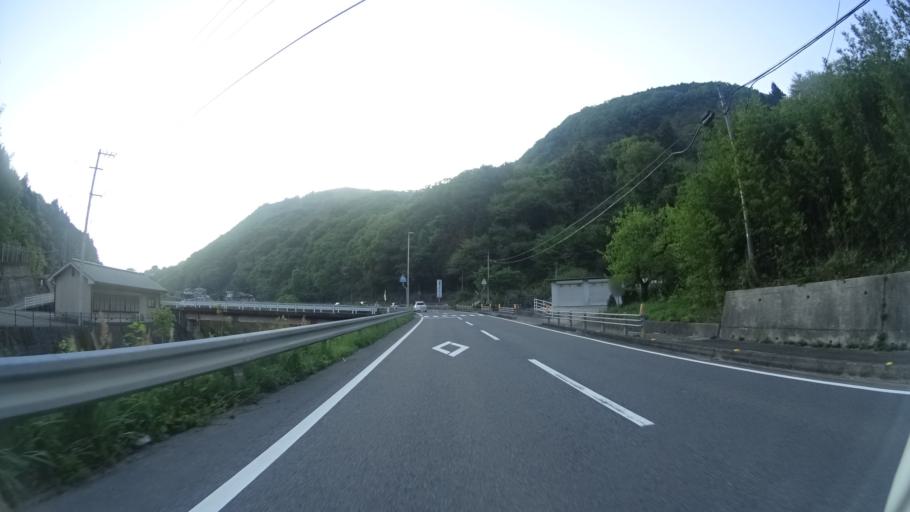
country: JP
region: Tokushima
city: Ikedacho
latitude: 34.0097
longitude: 133.7313
